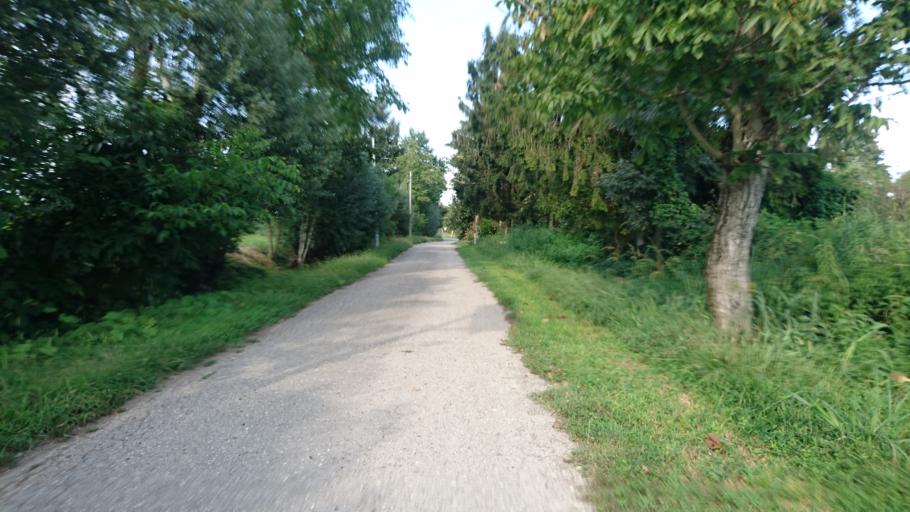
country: IT
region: Veneto
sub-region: Provincia di Padova
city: Selvazzano Dentro
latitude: 45.4007
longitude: 11.7867
